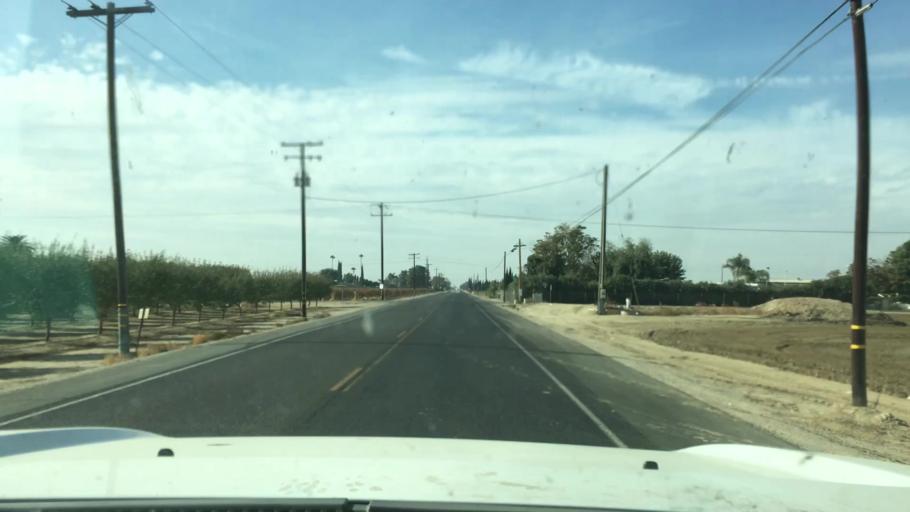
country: US
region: California
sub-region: Kern County
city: Shafter
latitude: 35.5000
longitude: -119.3126
